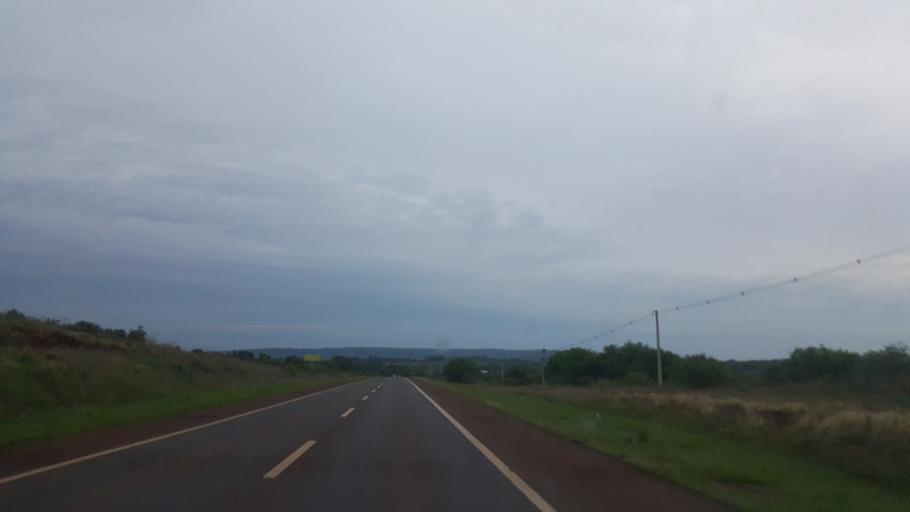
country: AR
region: Misiones
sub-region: Departamento de Apostoles
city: San Jose
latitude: -27.7707
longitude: -55.8050
